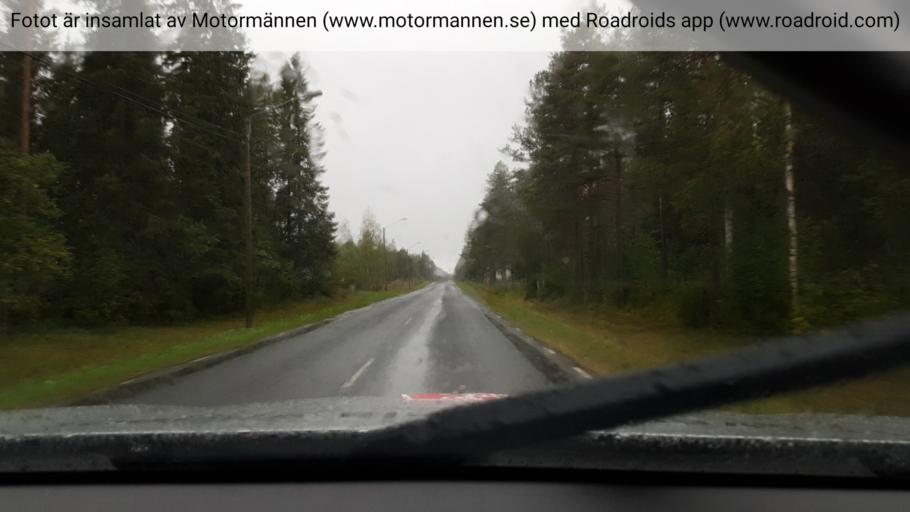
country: SE
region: Vaesterbotten
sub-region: Skelleftea Kommun
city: Storvik
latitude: 64.9716
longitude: 20.6857
